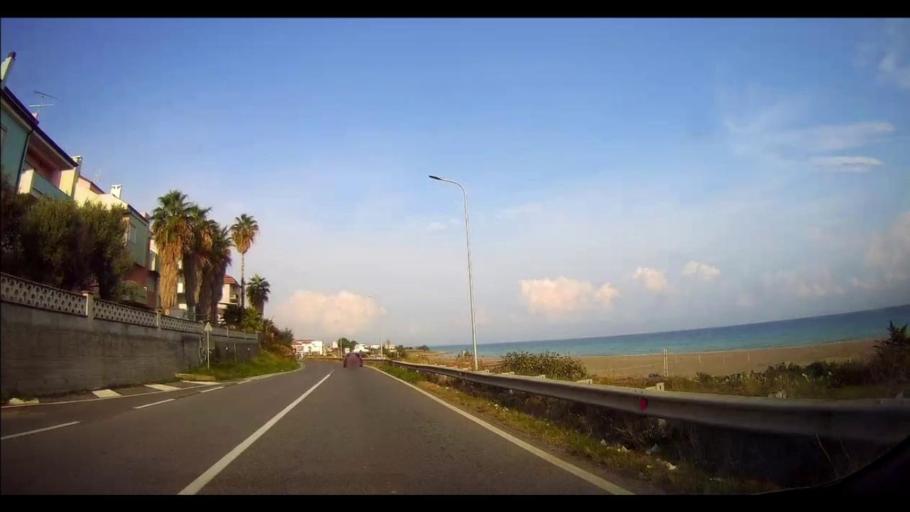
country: IT
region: Calabria
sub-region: Provincia di Cosenza
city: Cariati
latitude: 39.5079
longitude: 16.9345
